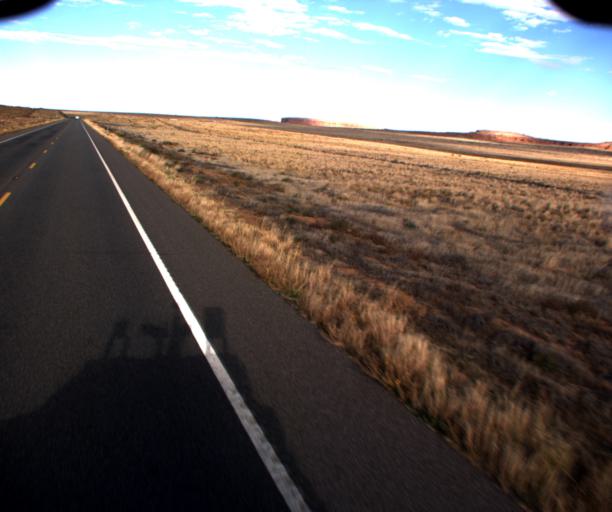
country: US
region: Arizona
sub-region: Apache County
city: Lukachukai
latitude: 36.9538
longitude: -109.2933
